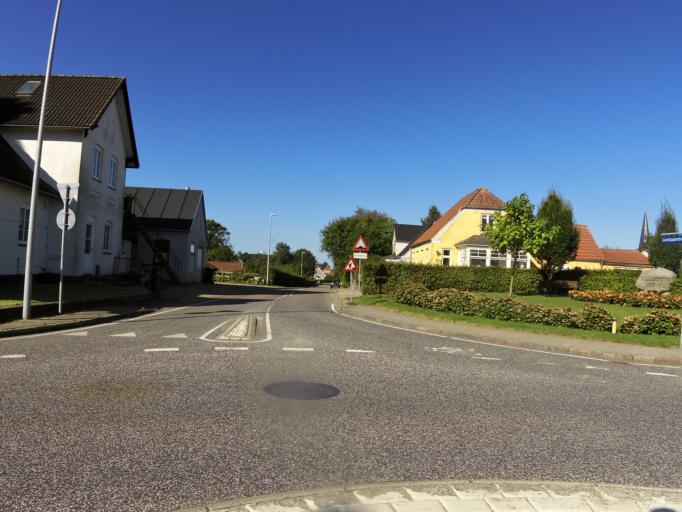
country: DK
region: South Denmark
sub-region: Sonderborg Kommune
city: Dybbol
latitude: 54.9466
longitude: 9.6963
